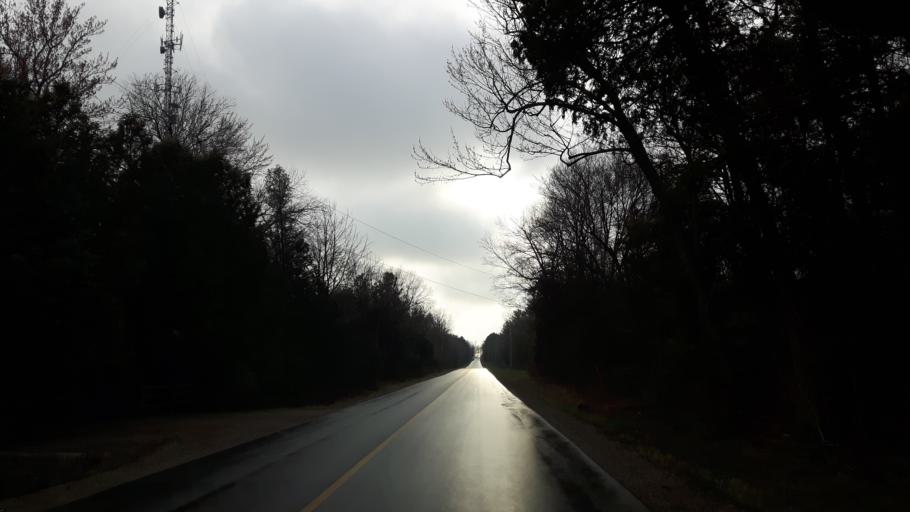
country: CA
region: Ontario
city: Bluewater
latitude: 43.5757
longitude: -81.6937
